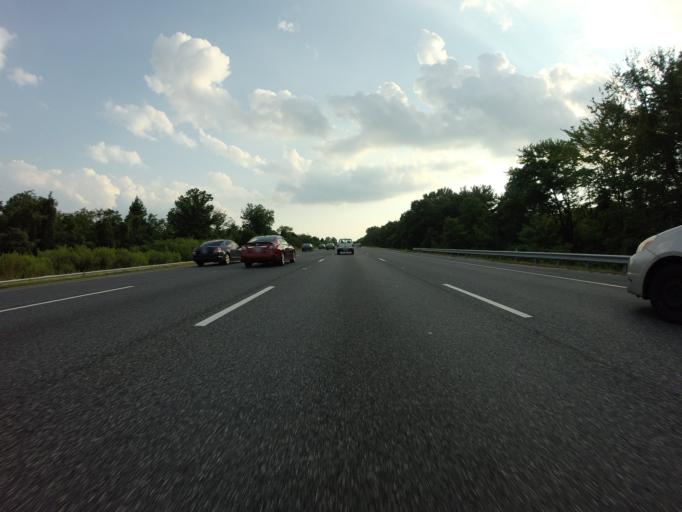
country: US
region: Maryland
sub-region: Howard County
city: Savage
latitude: 39.1684
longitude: -76.8070
